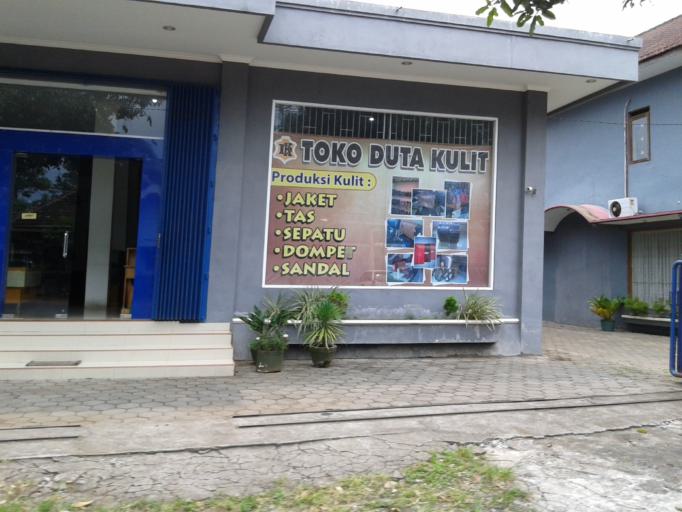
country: ID
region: East Java
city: Singosari
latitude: -7.9013
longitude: 112.6892
